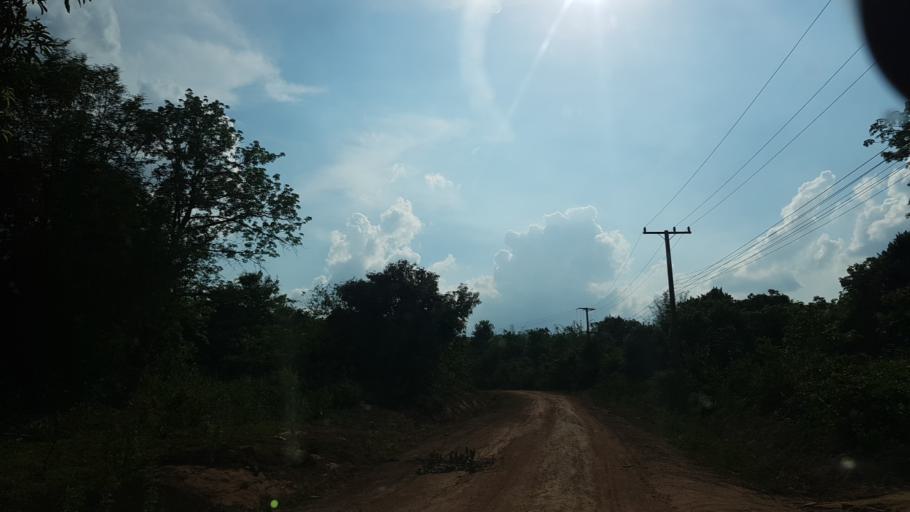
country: LA
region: Vientiane
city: Muang Phon-Hong
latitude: 18.3505
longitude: 102.2695
